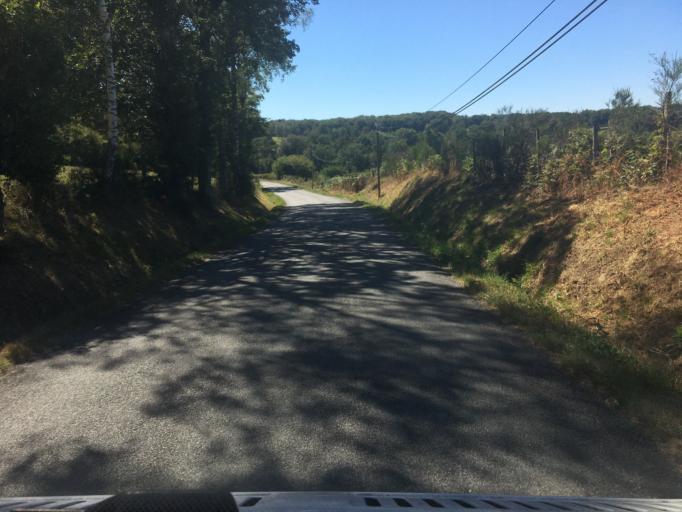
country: FR
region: Limousin
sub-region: Departement de la Correze
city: Bort-les-Orgues
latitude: 45.4426
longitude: 2.4766
